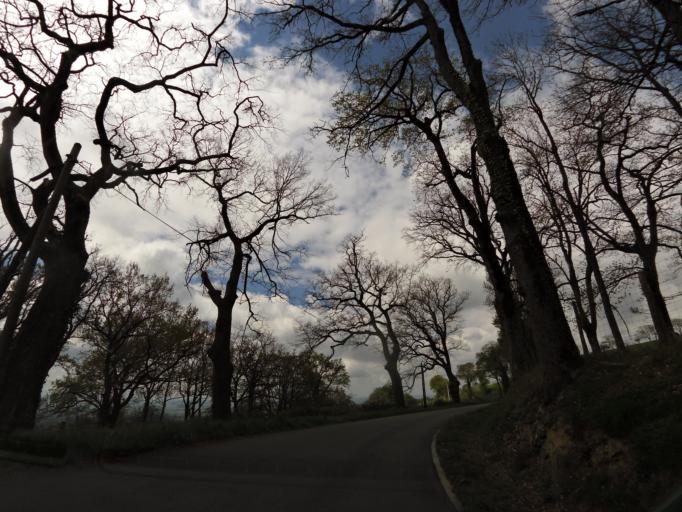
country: FR
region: Languedoc-Roussillon
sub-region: Departement de l'Aude
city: Alzonne
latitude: 43.3577
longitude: 2.1638
